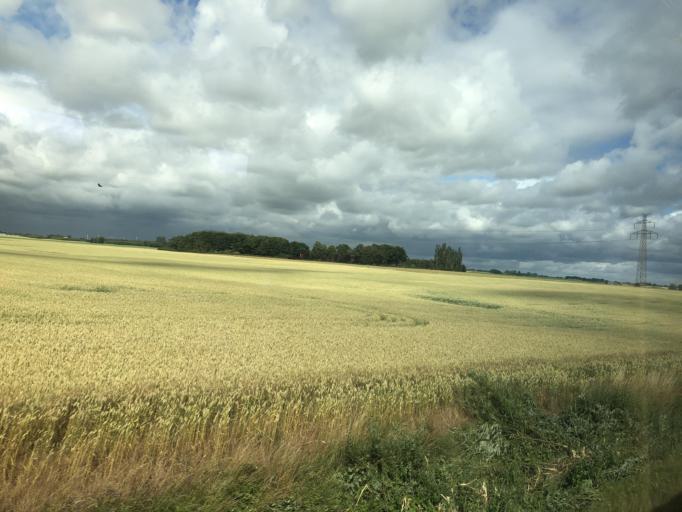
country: SE
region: Skane
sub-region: Landskrona
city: Asmundtorp
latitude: 55.8589
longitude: 12.9272
